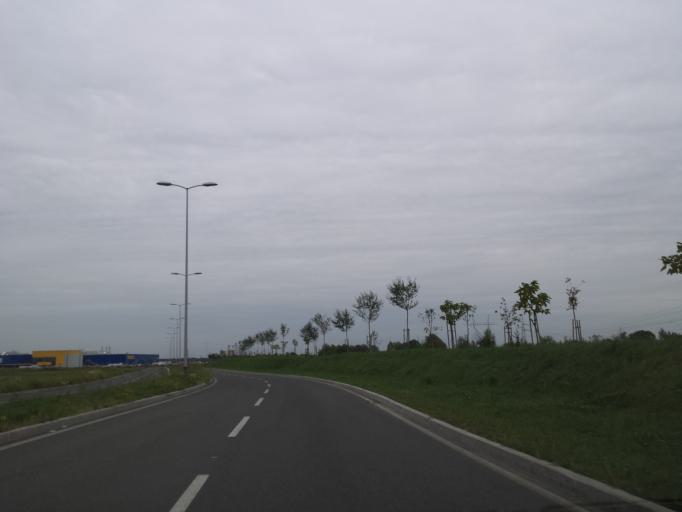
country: HR
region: Grad Zagreb
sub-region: Sesvete
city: Sesvete
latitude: 45.7927
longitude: 16.1477
